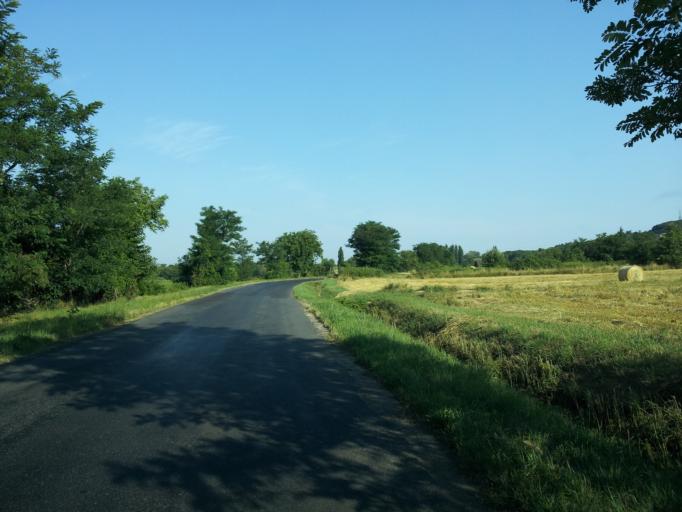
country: HU
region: Zala
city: Gyenesdias
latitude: 46.8549
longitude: 17.3275
